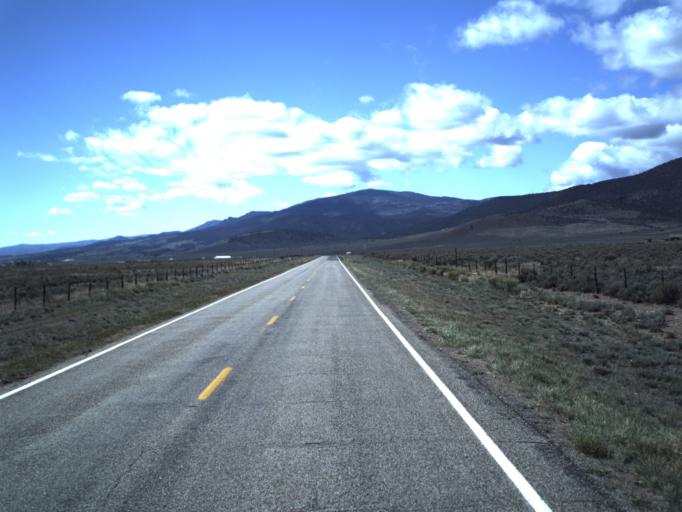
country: US
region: Utah
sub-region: Wayne County
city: Loa
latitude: 38.4805
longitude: -111.8954
